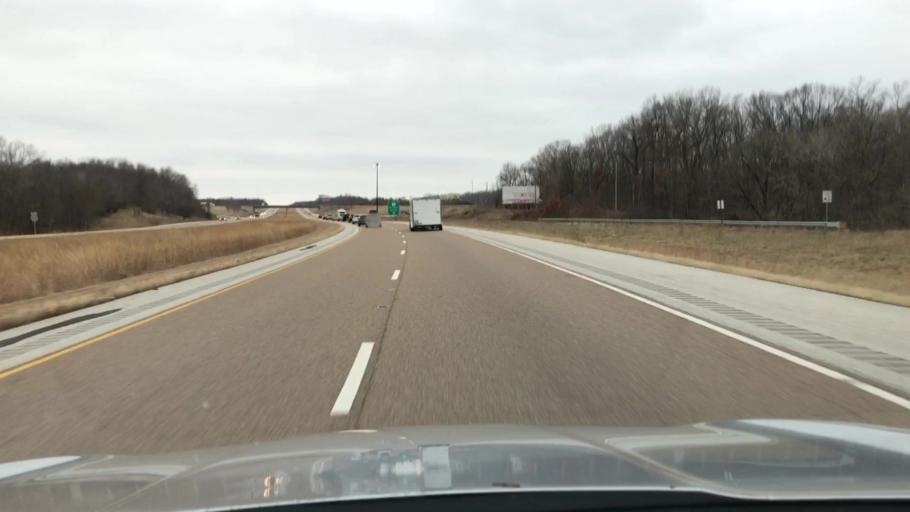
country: US
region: Illinois
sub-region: Macoupin County
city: Mount Olive
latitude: 39.0795
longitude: -89.7557
